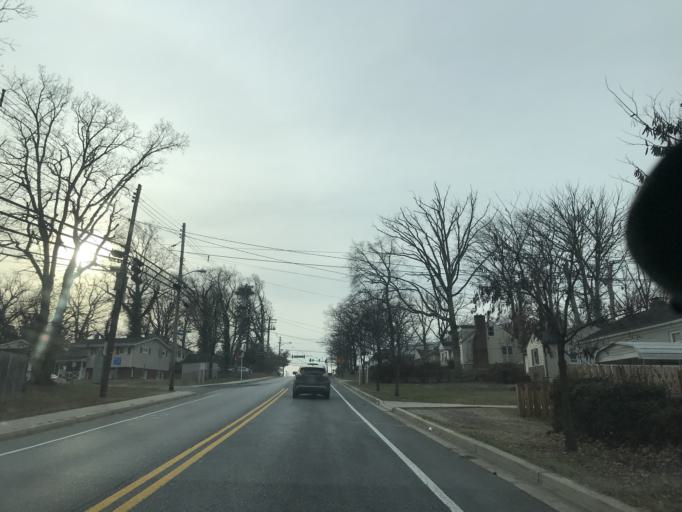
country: US
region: Maryland
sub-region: Prince George's County
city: Lanham
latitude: 38.9552
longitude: -76.8580
